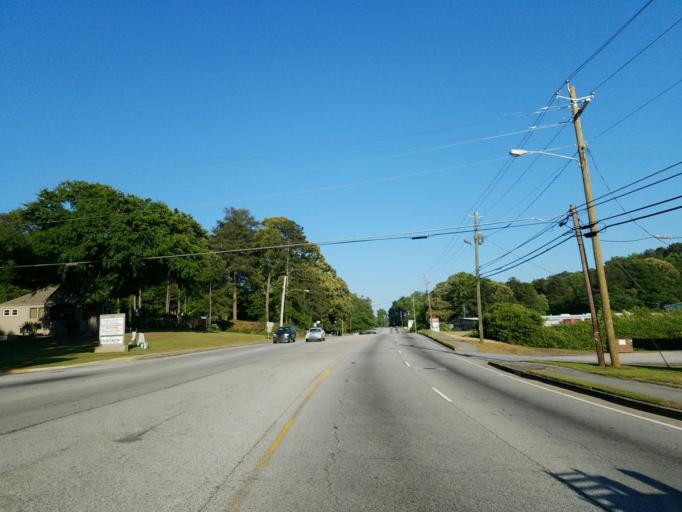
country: US
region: Georgia
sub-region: Cobb County
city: Mableton
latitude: 33.8175
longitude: -84.6068
